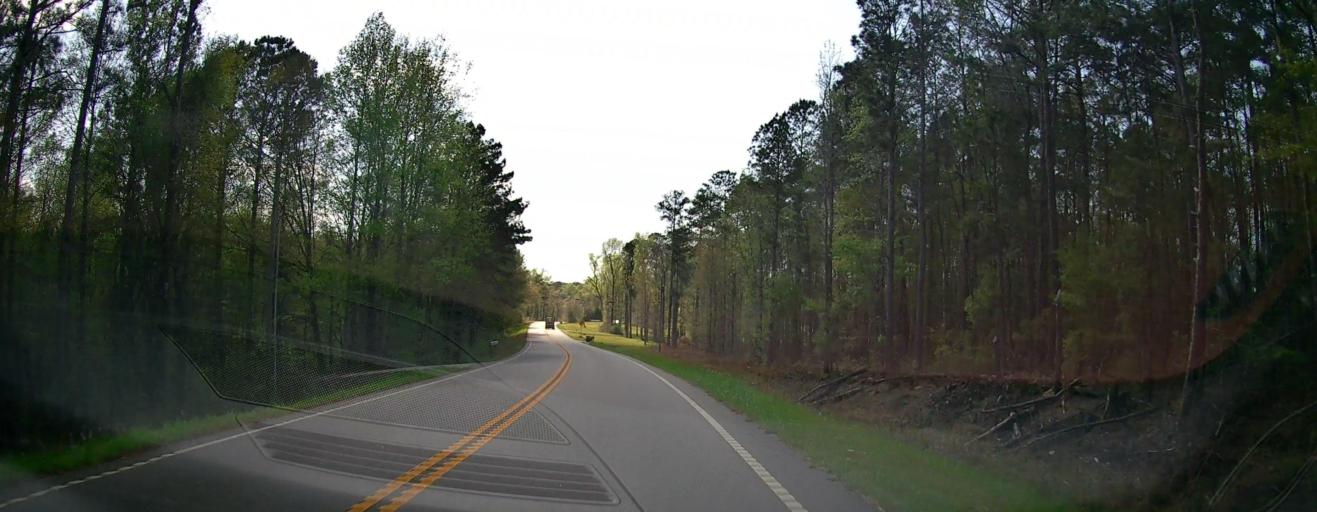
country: US
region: Georgia
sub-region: Baldwin County
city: Hardwick
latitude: 33.0801
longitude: -83.1491
